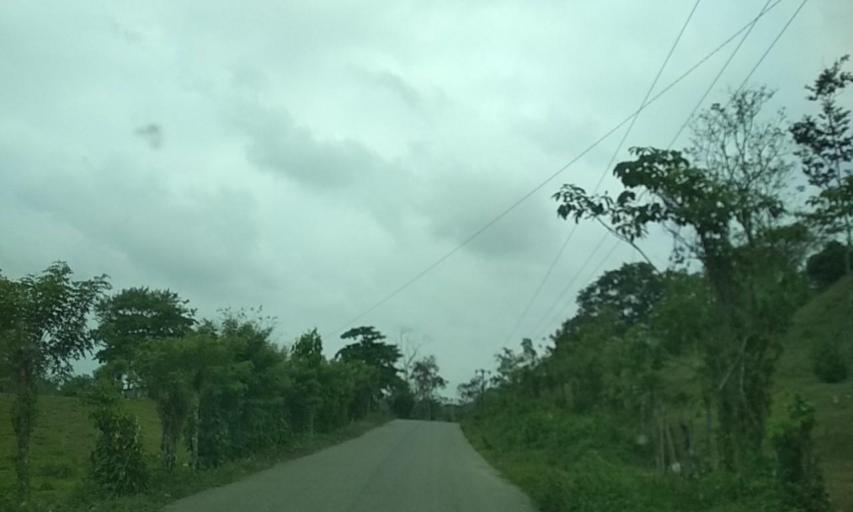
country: MX
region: Veracruz
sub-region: Uxpanapa
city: Poblado 10
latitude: 17.4636
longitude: -94.1081
